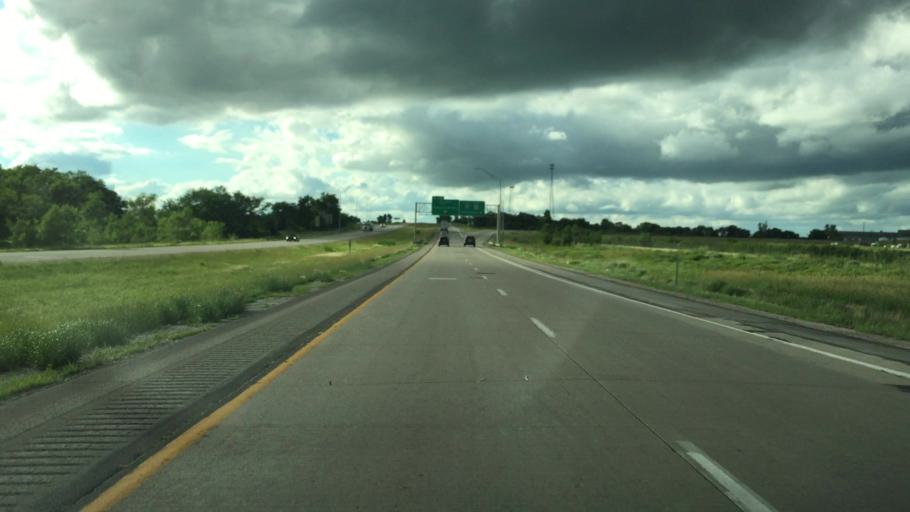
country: US
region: Iowa
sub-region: Polk County
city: Altoona
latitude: 41.6531
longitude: -93.5166
